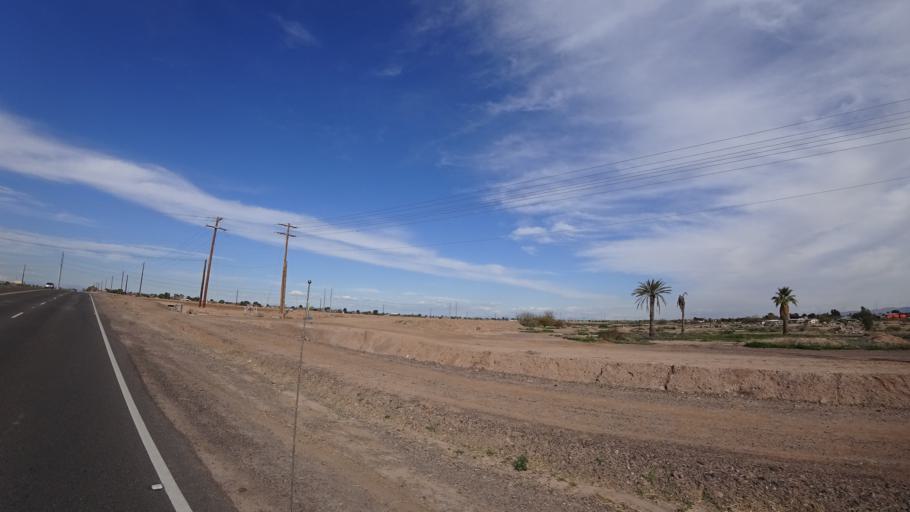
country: US
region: Arizona
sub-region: Maricopa County
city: Avondale
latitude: 33.4092
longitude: -112.3062
